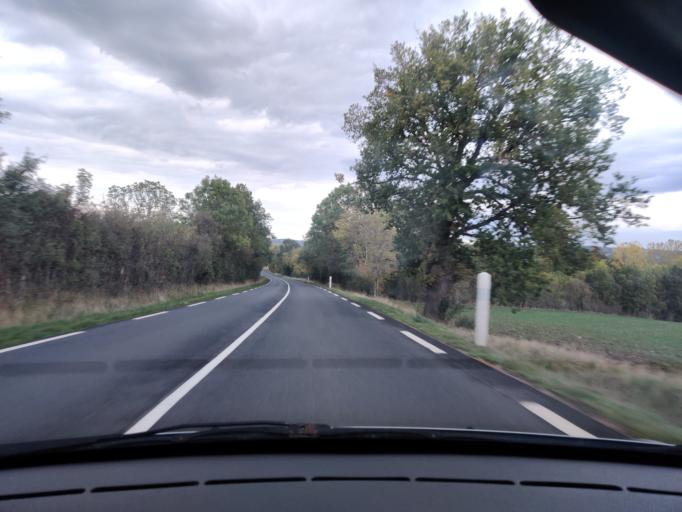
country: FR
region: Auvergne
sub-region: Departement du Puy-de-Dome
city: Combronde
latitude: 46.0052
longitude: 3.0936
